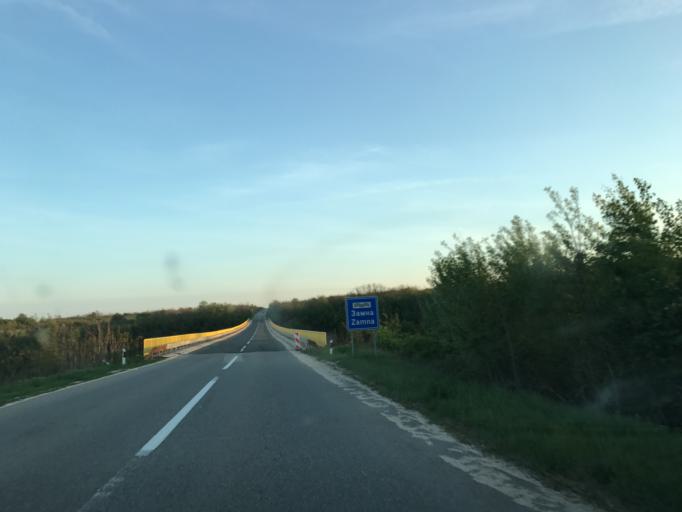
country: RO
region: Mehedinti
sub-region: Comuna Gogosu
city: Ostrovu Mare
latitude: 44.3709
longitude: 22.4803
